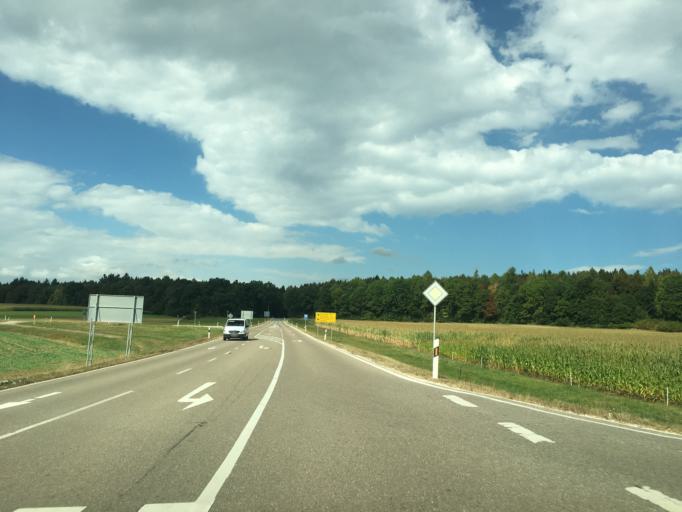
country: DE
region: Baden-Wuerttemberg
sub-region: Tuebingen Region
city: Hayingen
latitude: 48.2973
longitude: 9.4570
